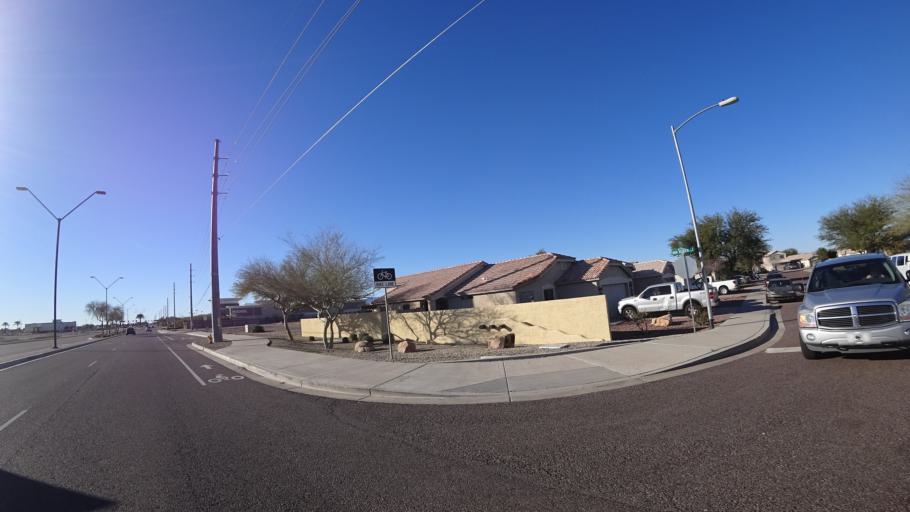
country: US
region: Arizona
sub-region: Maricopa County
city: Goodyear
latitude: 33.4500
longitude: -112.3876
